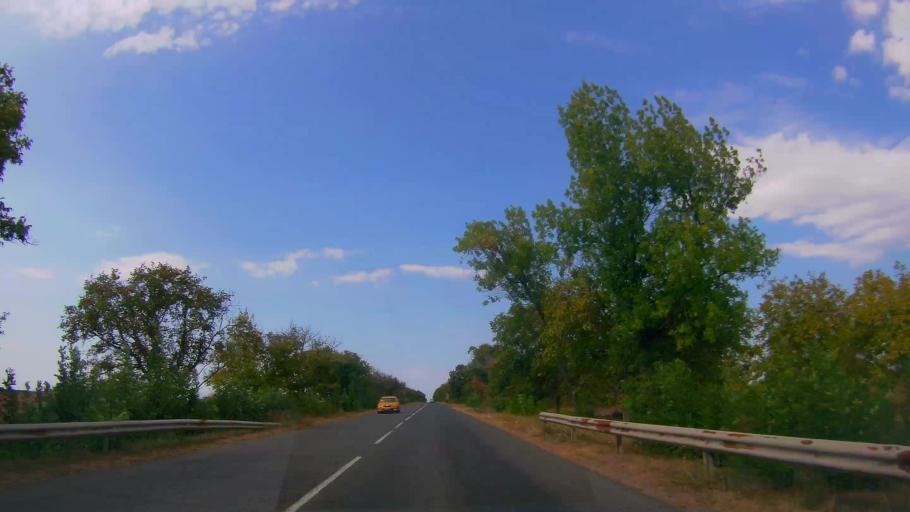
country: BG
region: Burgas
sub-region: Obshtina Aytos
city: Aytos
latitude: 42.6844
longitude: 27.1340
